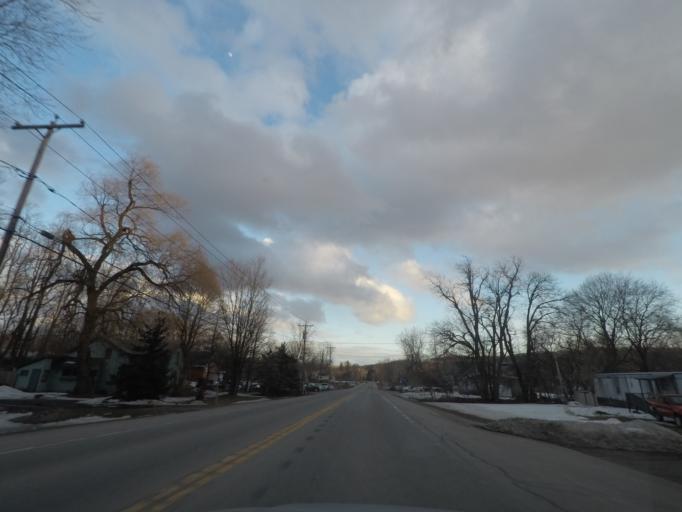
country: US
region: New York
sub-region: Montgomery County
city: Saint Johnsville
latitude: 43.0022
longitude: -74.7035
